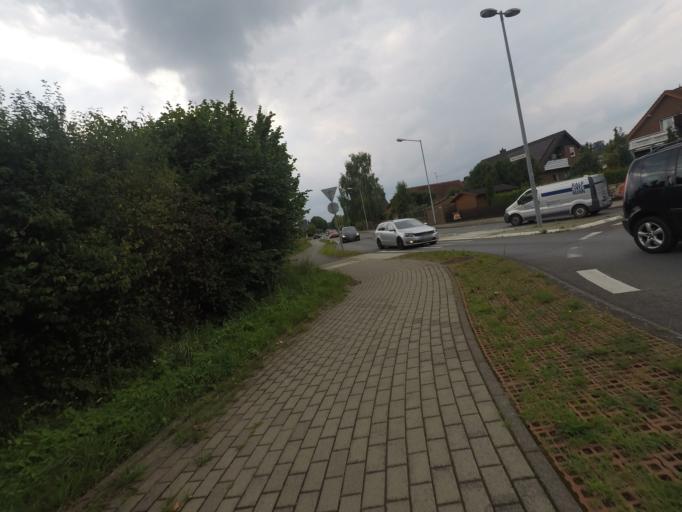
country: DE
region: North Rhine-Westphalia
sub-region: Regierungsbezirk Detmold
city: Hiddenhausen
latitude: 52.1409
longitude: 8.6186
